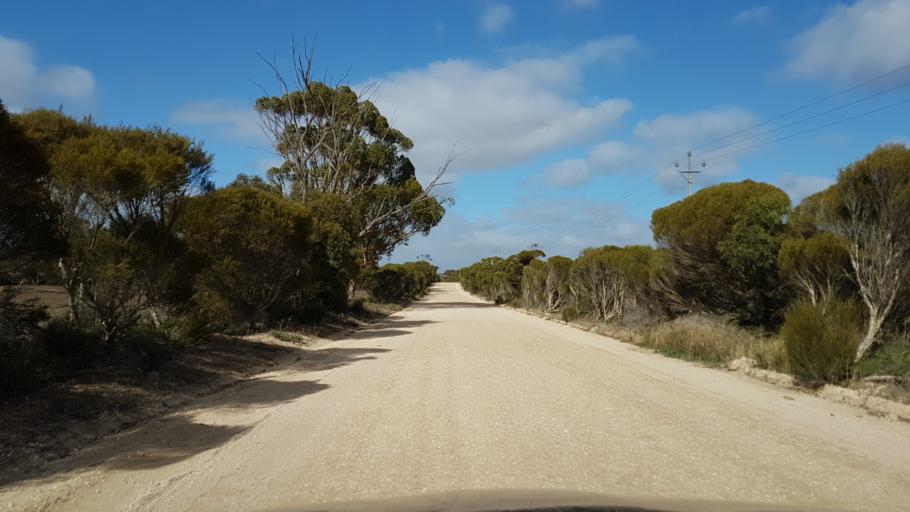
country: AU
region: South Australia
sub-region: Murray Bridge
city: Murray Bridge
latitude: -35.1146
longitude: 139.1952
